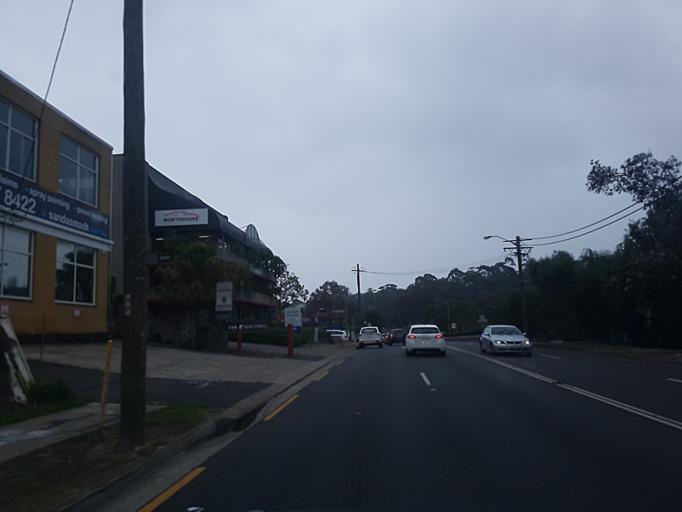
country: AU
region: New South Wales
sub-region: Willoughby
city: Castle Cove
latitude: -33.7875
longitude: 151.2017
